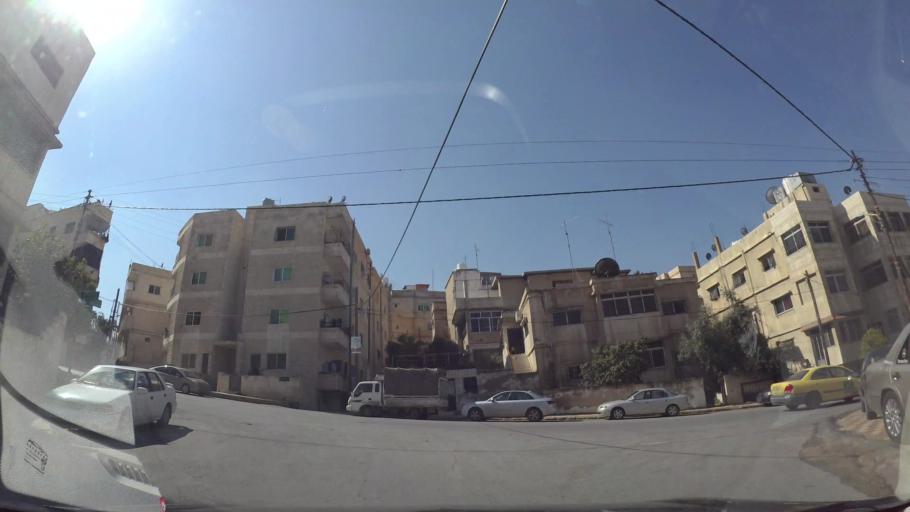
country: JO
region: Amman
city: Amman
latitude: 31.9814
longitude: 35.9835
